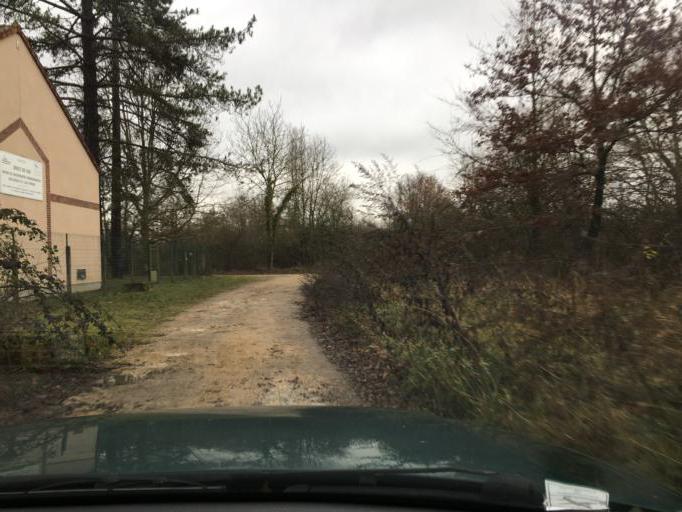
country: FR
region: Centre
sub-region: Departement du Loiret
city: Olivet
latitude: 47.8468
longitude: 1.8764
